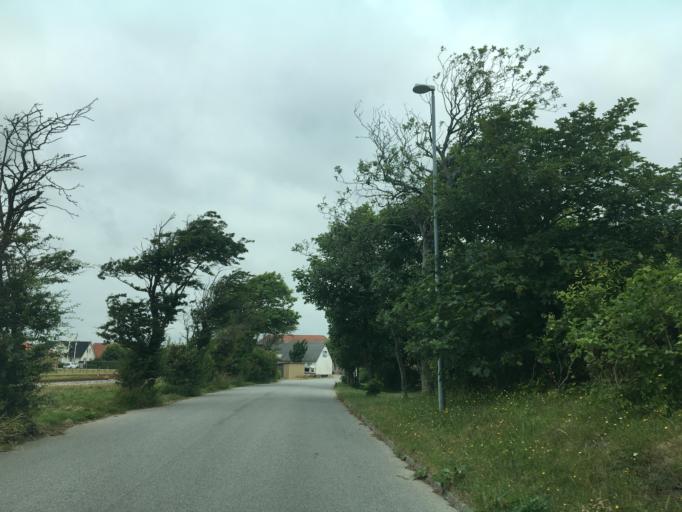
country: DK
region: North Denmark
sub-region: Thisted Kommune
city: Hurup
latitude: 56.7517
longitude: 8.4187
